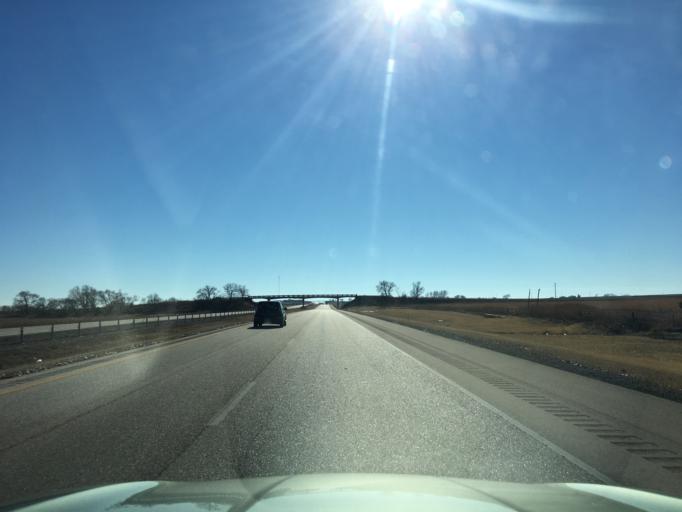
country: US
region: Oklahoma
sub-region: Kay County
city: Blackwell
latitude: 36.8866
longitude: -97.3525
